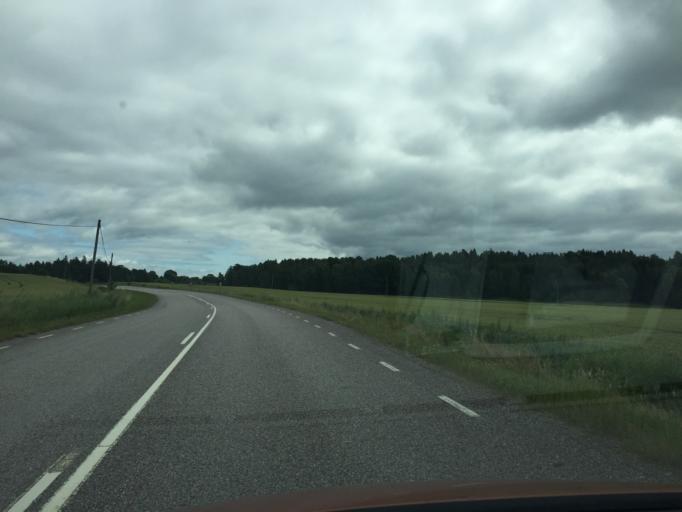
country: SE
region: Soedermanland
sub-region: Trosa Kommun
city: Vagnharad
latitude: 58.9871
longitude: 17.6303
